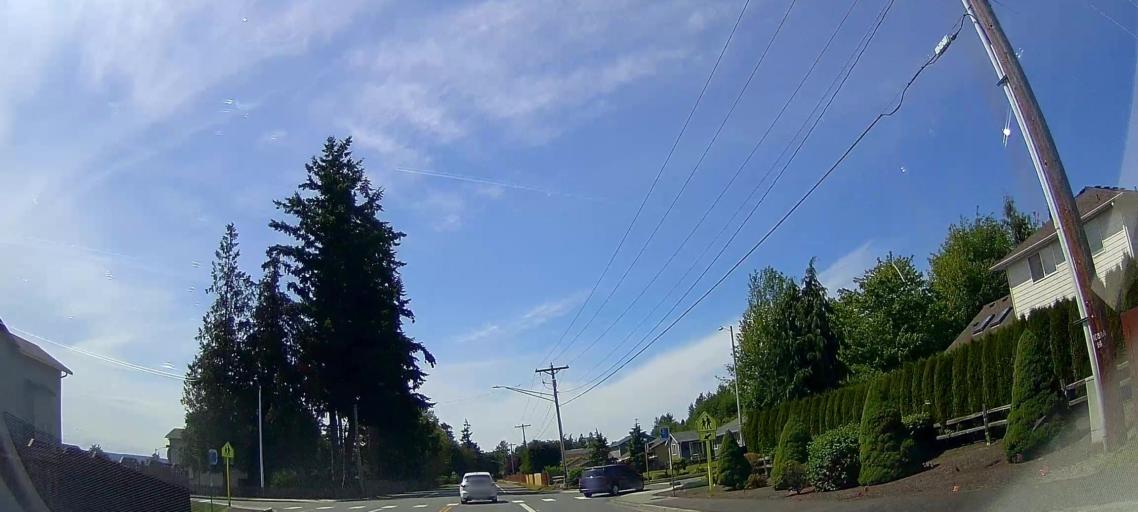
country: US
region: Washington
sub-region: Snohomish County
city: Stanwood
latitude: 48.2342
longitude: -122.3379
